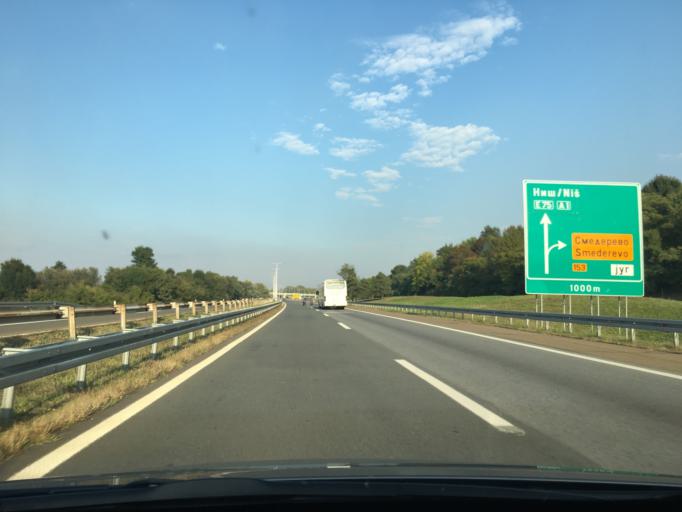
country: RS
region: Central Serbia
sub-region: Podunavski Okrug
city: Smederevo
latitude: 44.5810
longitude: 20.9509
